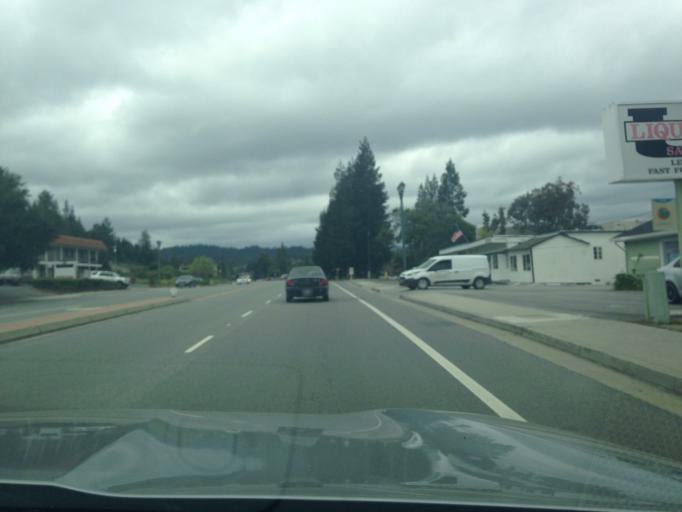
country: US
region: California
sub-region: Santa Cruz County
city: Scotts Valley
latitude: 37.0513
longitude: -122.0145
